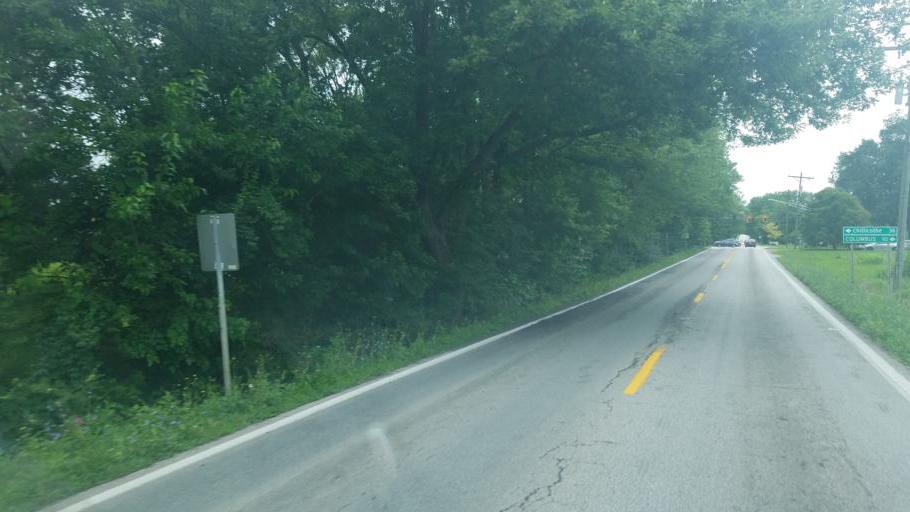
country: US
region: Ohio
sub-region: Pickaway County
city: Commercial Point
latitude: 39.8252
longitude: -83.0307
